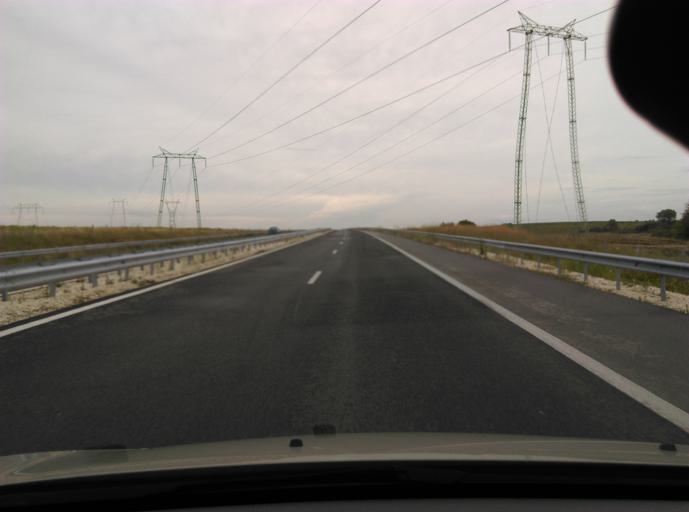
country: BG
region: Stara Zagora
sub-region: Obshtina Chirpan
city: Chirpan
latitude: 42.1293
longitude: 25.3631
